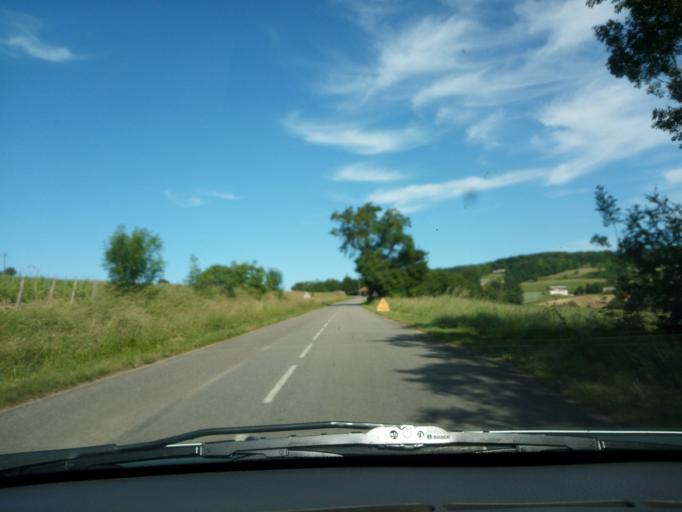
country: FR
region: Midi-Pyrenees
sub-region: Departement du Lot
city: Castelnau-Montratier
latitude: 44.2624
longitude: 1.3581
